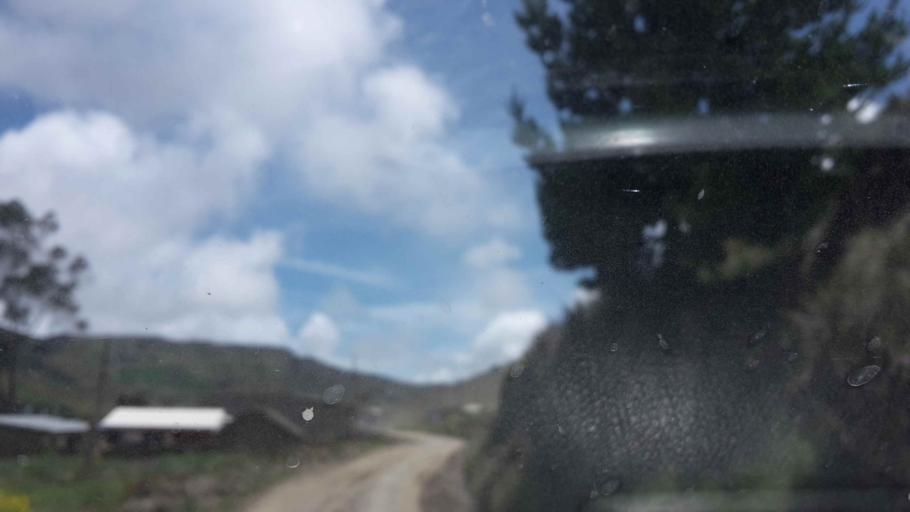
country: BO
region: Cochabamba
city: Cochabamba
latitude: -17.1976
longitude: -66.0832
